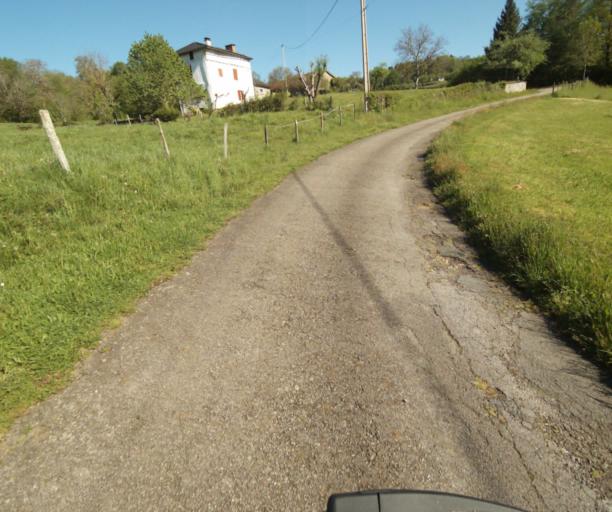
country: FR
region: Limousin
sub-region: Departement de la Correze
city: Tulle
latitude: 45.2790
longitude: 1.7789
